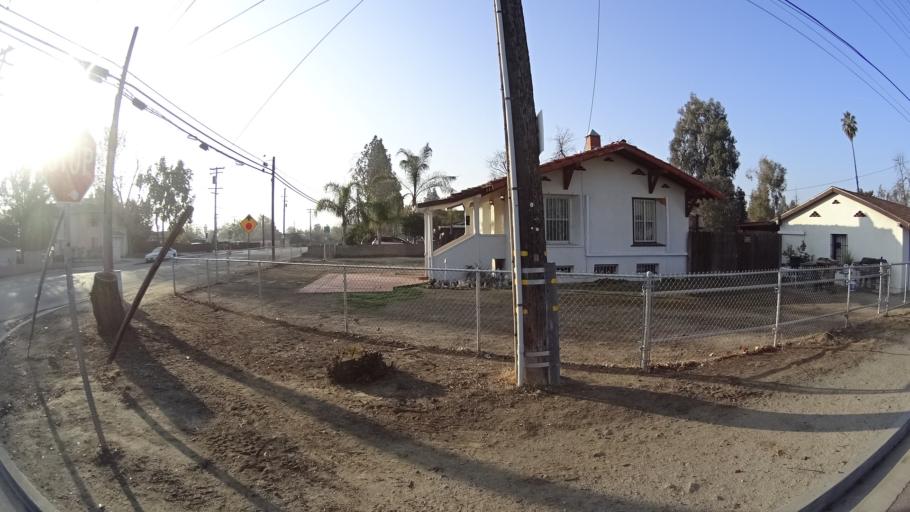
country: US
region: California
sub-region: Kern County
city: Bakersfield
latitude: 35.3625
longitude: -119.0436
